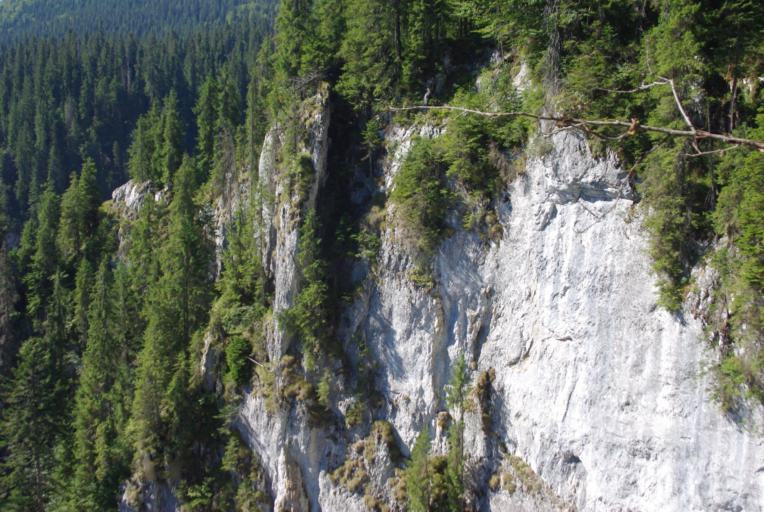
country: RO
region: Alba
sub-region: Comuna Arieseni
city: Arieseni
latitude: 46.5651
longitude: 22.7009
